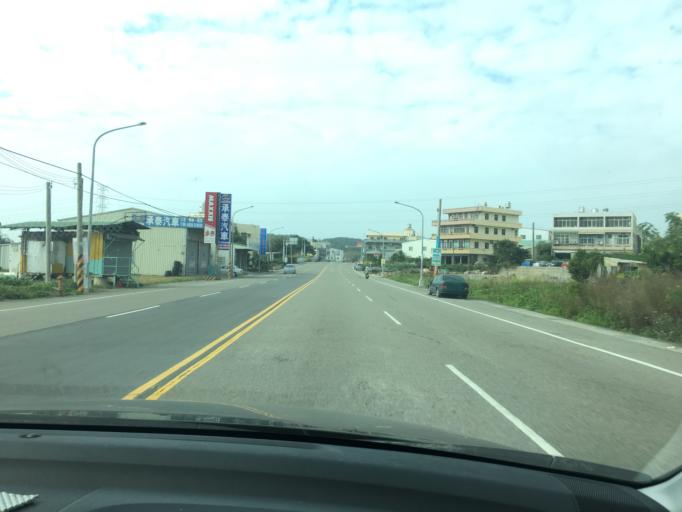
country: TW
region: Taiwan
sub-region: Miaoli
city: Miaoli
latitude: 24.4966
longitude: 120.6976
